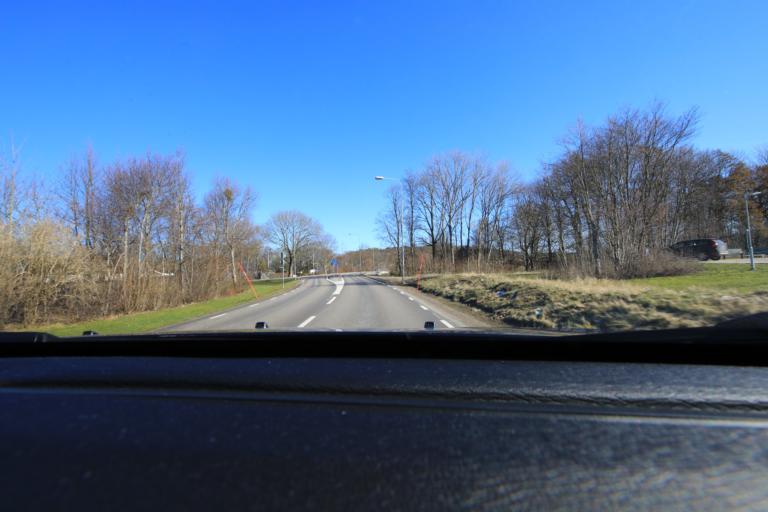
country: SE
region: Halland
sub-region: Varbergs Kommun
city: Tvaaker
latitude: 57.0429
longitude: 12.4071
